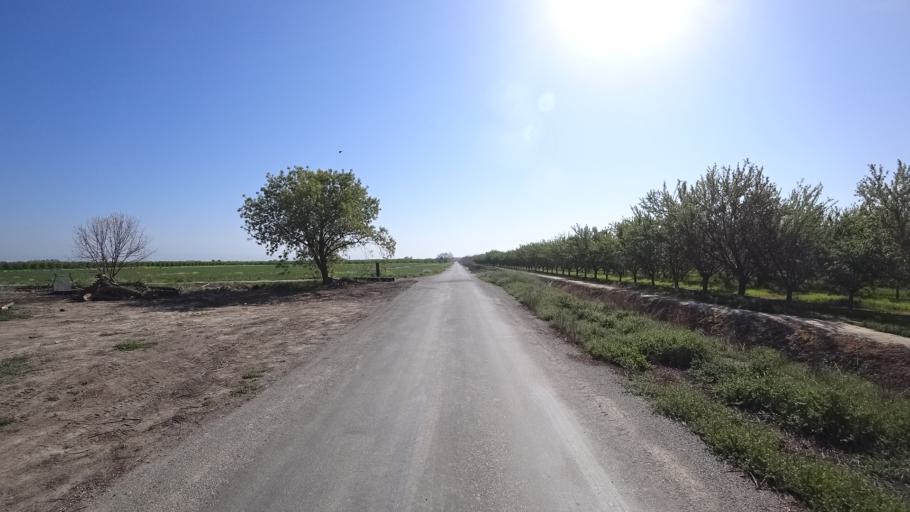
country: US
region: California
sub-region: Glenn County
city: Hamilton City
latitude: 39.6378
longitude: -122.0265
